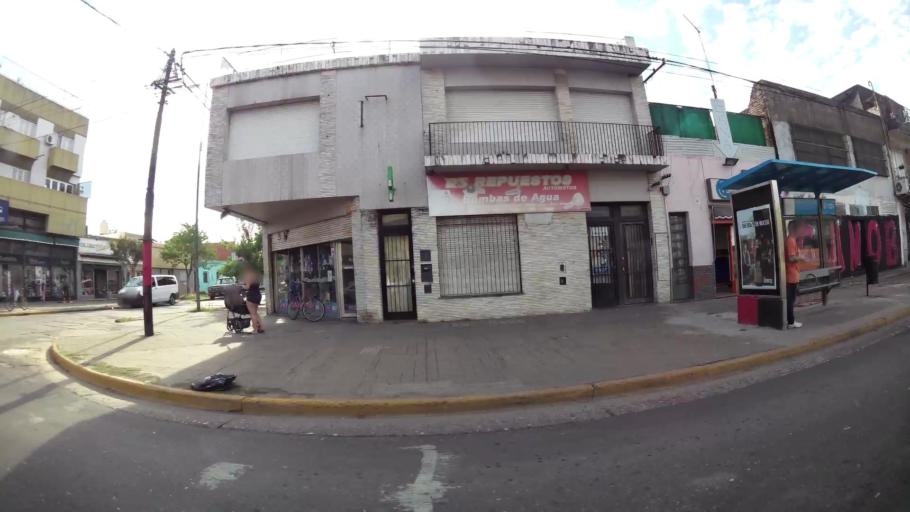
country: AR
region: Santa Fe
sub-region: Departamento de Rosario
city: Rosario
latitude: -32.9771
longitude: -60.6700
